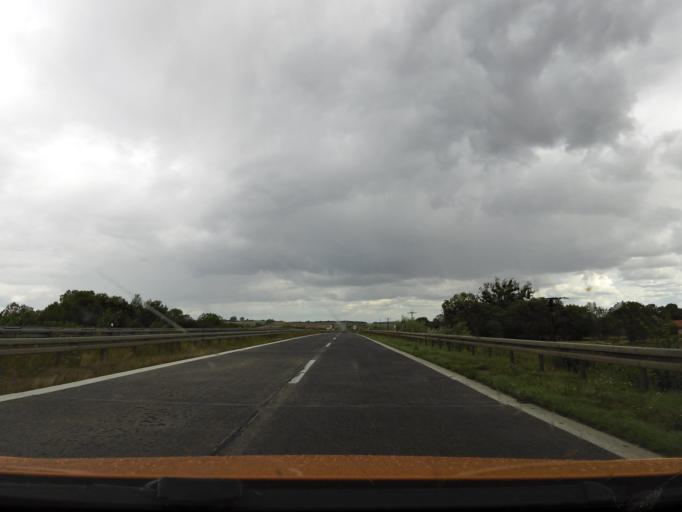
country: DE
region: Brandenburg
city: Gramzow
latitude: 53.2781
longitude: 14.0662
